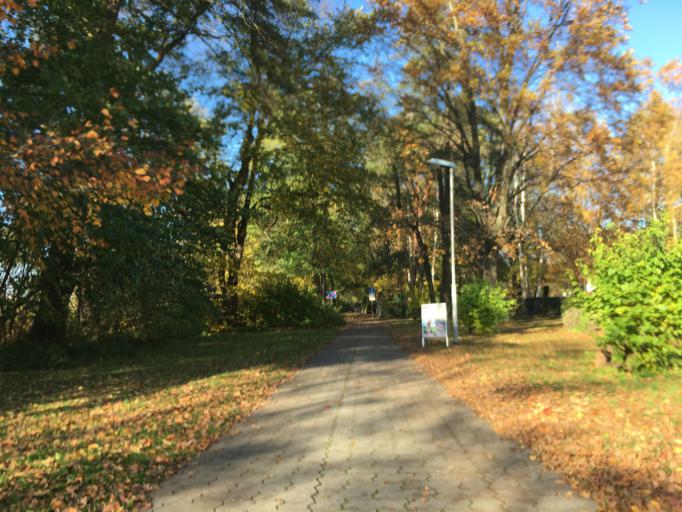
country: DE
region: Brandenburg
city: Bad Saarow
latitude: 52.2608
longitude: 14.0703
